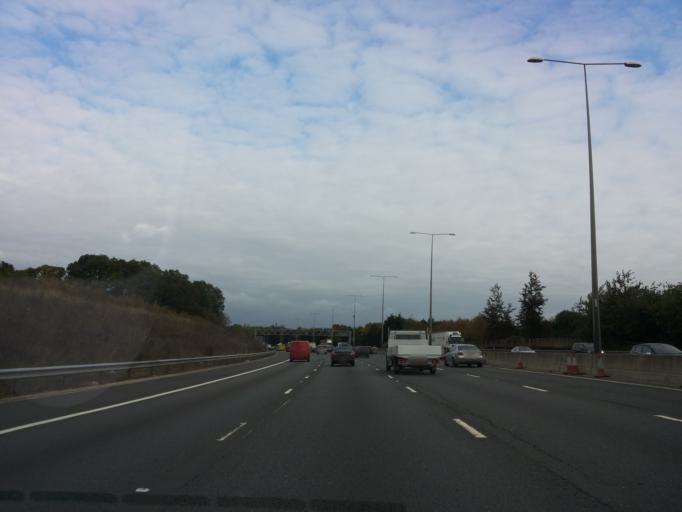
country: GB
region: England
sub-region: Hertfordshire
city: Chorleywood
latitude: 51.6733
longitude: -0.4686
